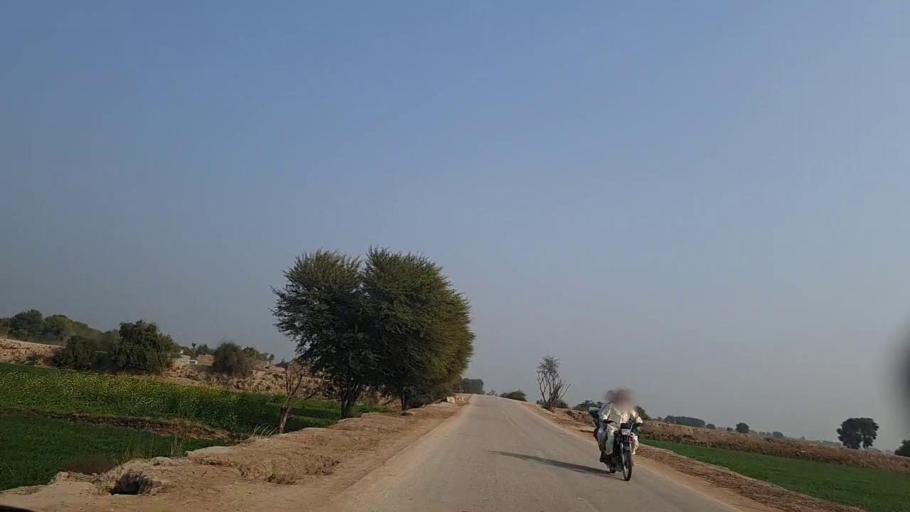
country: PK
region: Sindh
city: Sann
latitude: 26.1475
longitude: 68.1345
